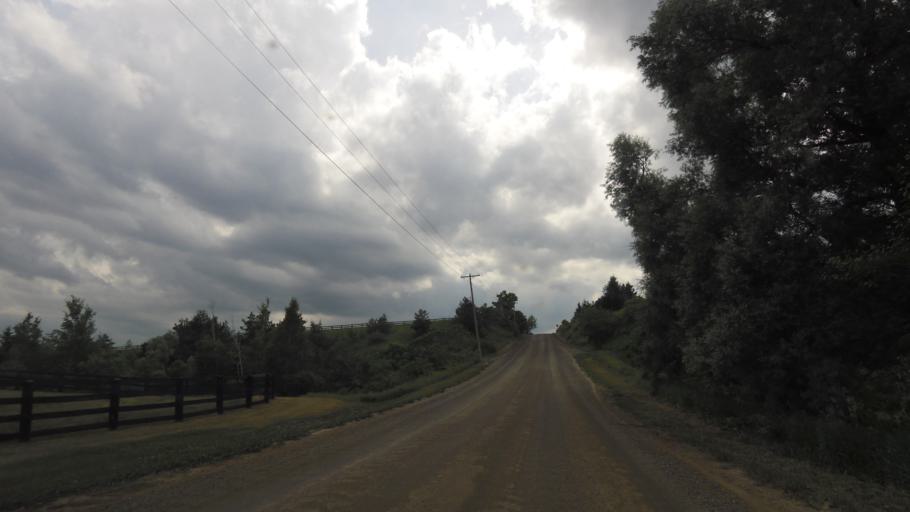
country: CA
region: Ontario
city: Orangeville
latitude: 43.8623
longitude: -79.9449
